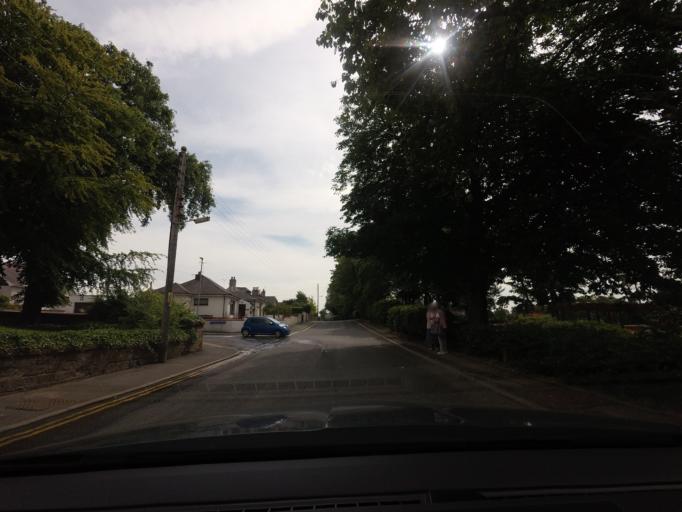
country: GB
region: Scotland
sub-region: Aberdeenshire
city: Turriff
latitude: 57.5367
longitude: -2.4506
